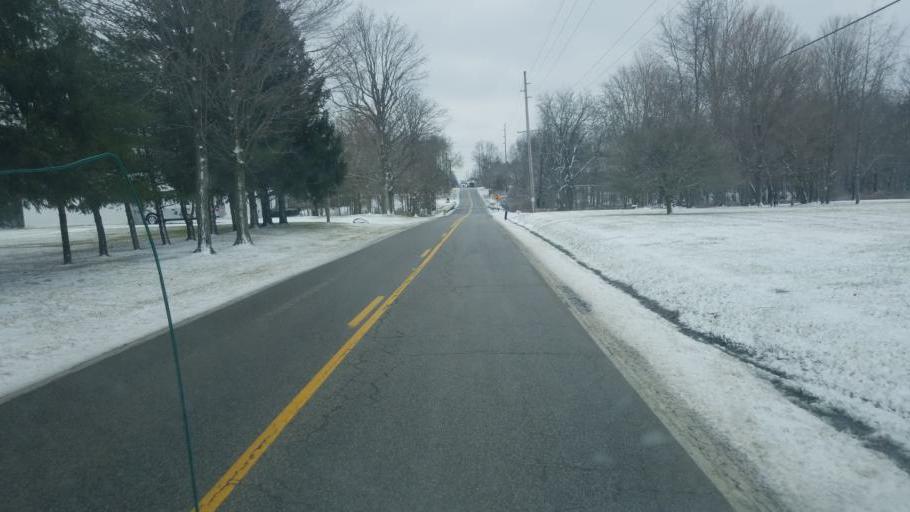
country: US
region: Ohio
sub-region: Delaware County
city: Sunbury
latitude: 40.2678
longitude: -82.7874
